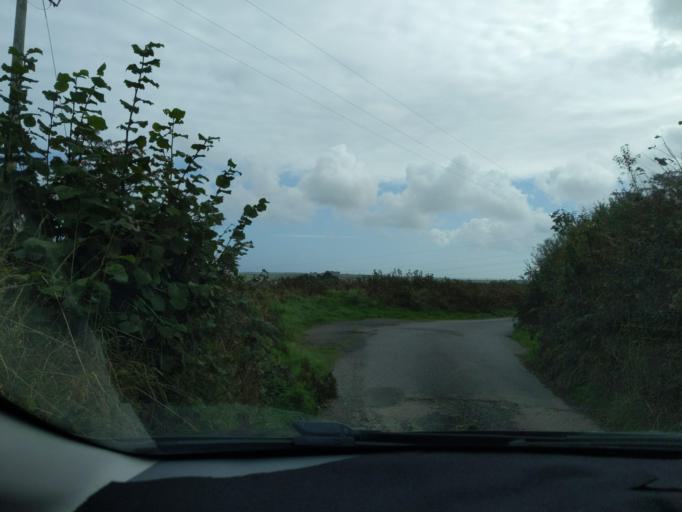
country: GB
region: England
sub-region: Cornwall
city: Par
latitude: 50.3882
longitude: -4.7028
